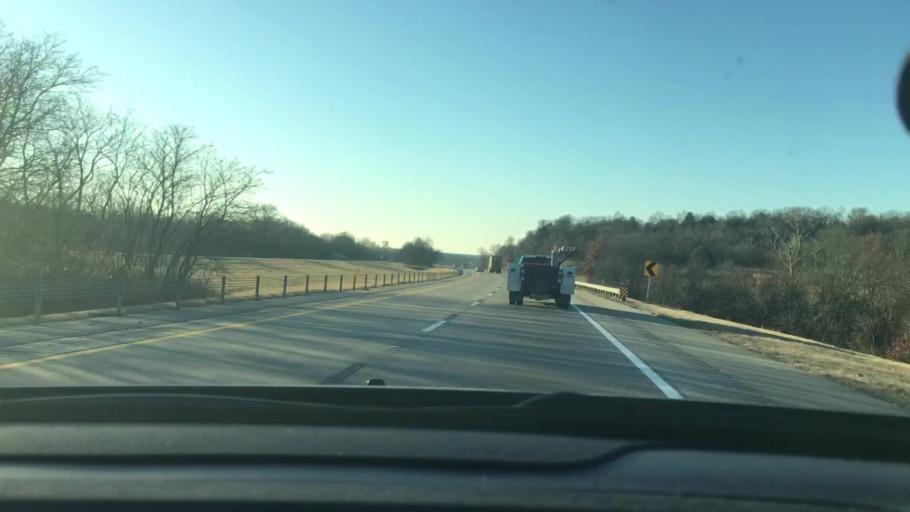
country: US
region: Oklahoma
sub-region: Murray County
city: Davis
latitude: 34.3555
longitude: -97.1492
